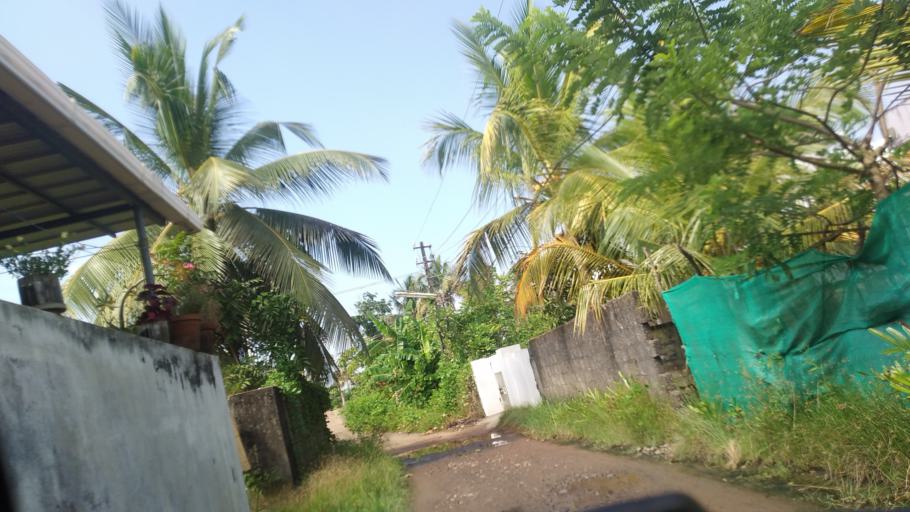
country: IN
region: Kerala
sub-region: Ernakulam
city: Elur
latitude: 10.0788
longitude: 76.2046
